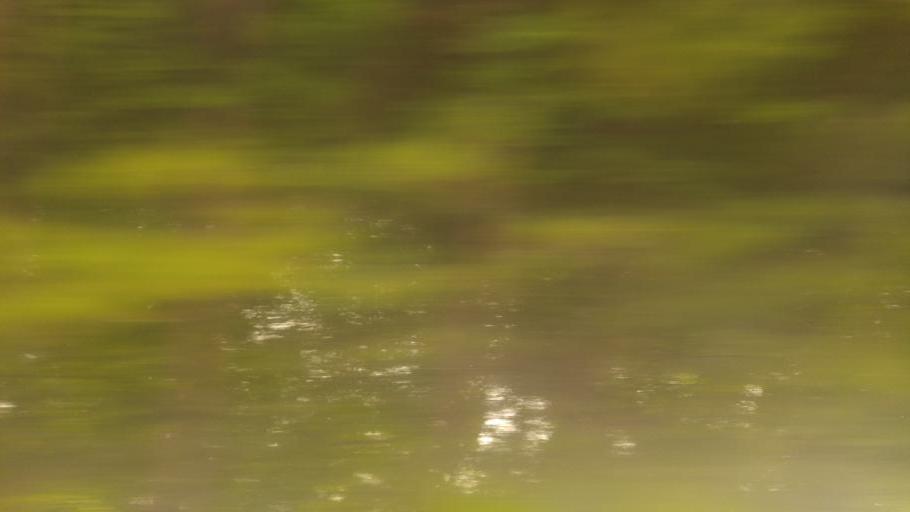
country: US
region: Virginia
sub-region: Henrico County
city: Laurel
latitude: 37.6439
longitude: -77.5075
